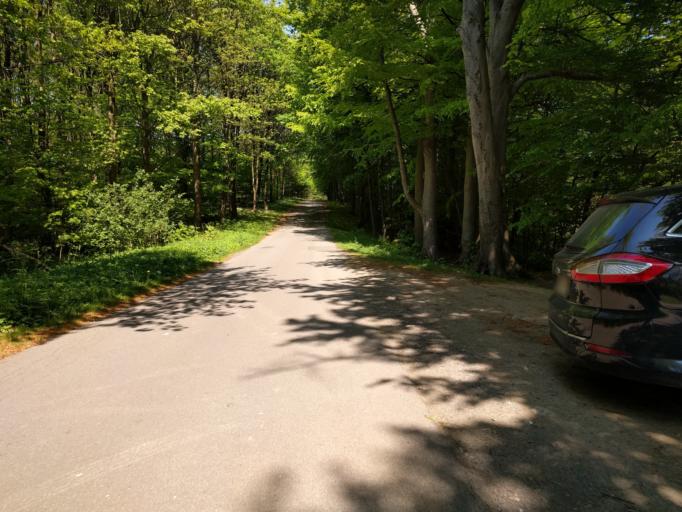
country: DK
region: Zealand
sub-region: Guldborgsund Kommune
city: Stubbekobing
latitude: 54.8182
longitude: 12.1298
